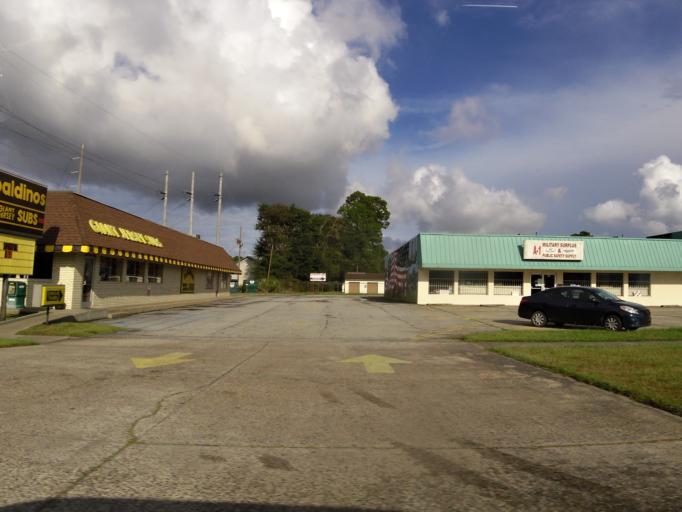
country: US
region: Georgia
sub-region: Liberty County
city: Hinesville
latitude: 31.8526
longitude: -81.6062
